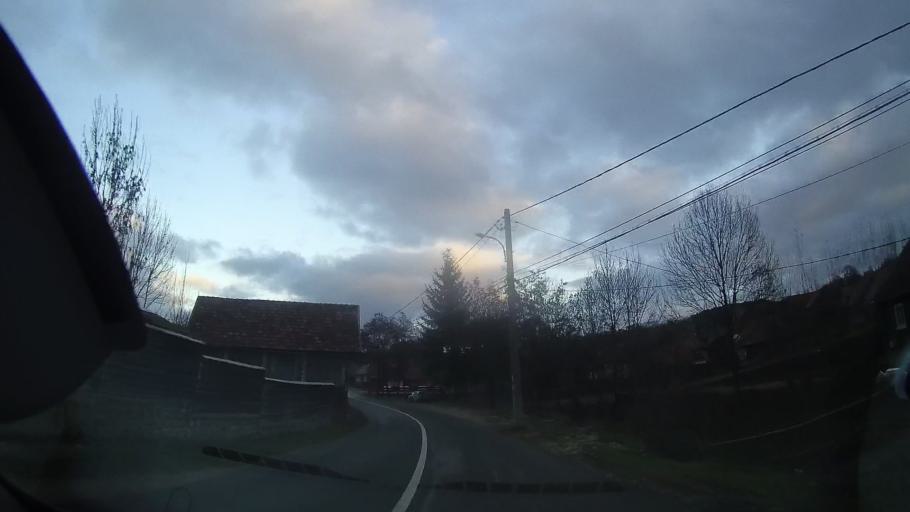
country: RO
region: Cluj
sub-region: Comuna Manastireni
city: Manastireni
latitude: 46.7817
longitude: 23.0871
